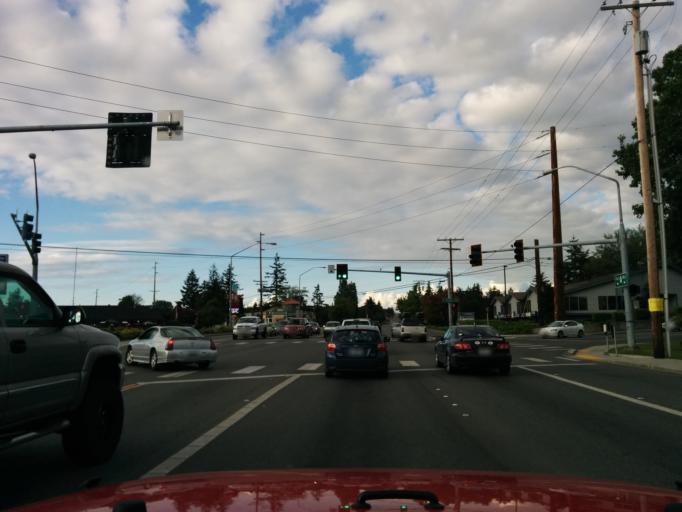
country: US
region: Washington
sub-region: Island County
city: Oak Harbor
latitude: 48.2982
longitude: -122.6530
